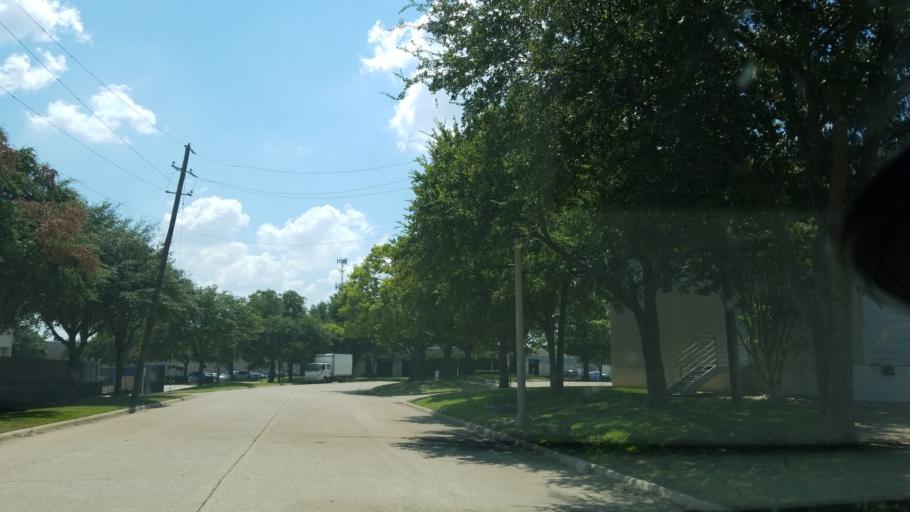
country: US
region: Texas
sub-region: Dallas County
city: Richardson
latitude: 32.8918
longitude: -96.7027
